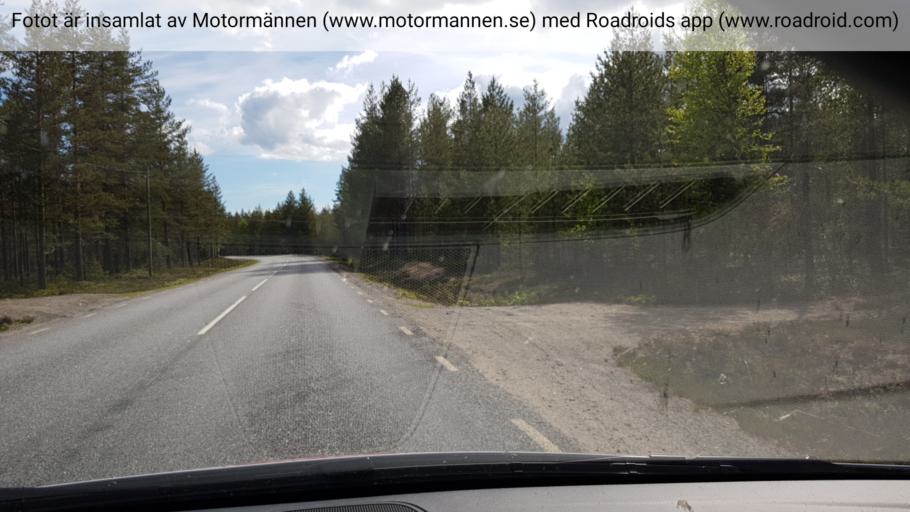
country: SE
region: Vaesterbotten
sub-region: Umea Kommun
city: Saevar
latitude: 64.0026
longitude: 20.4937
